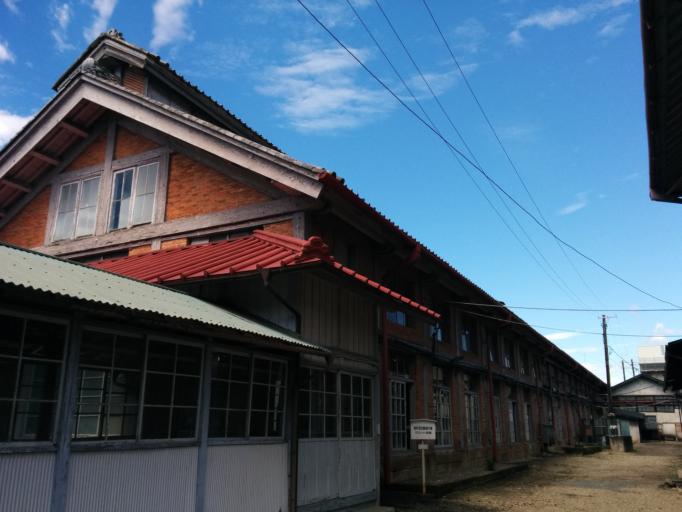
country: JP
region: Gunma
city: Tomioka
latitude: 36.2552
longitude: 138.8883
